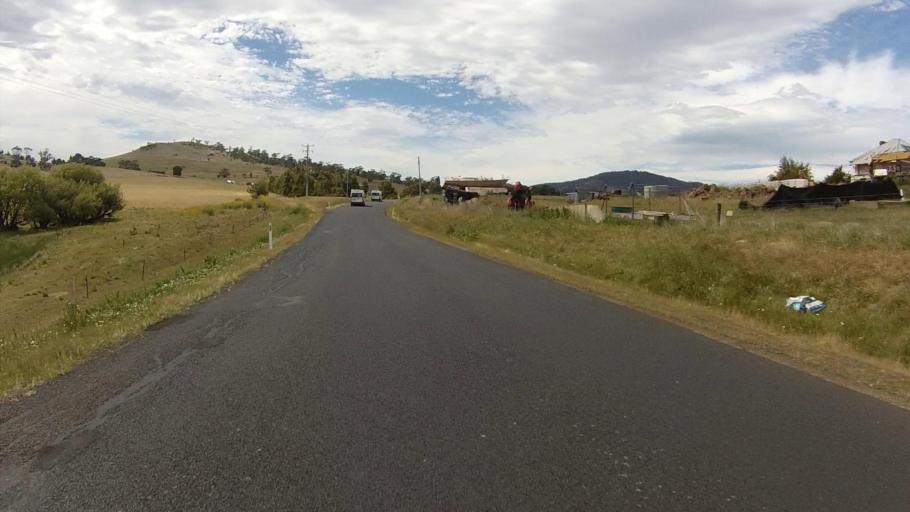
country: AU
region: Tasmania
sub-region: Brighton
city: Old Beach
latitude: -42.7032
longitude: 147.3099
